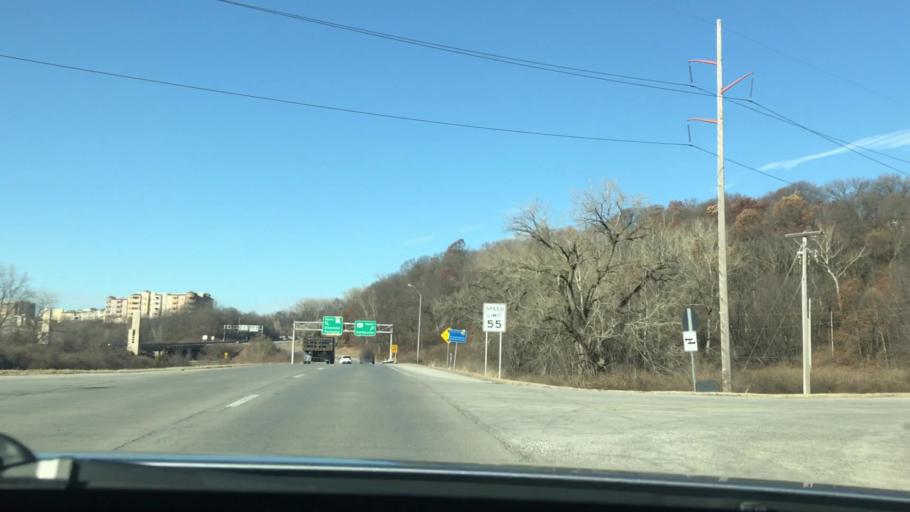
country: US
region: Missouri
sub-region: Platte County
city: Riverside
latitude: 39.1584
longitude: -94.5872
